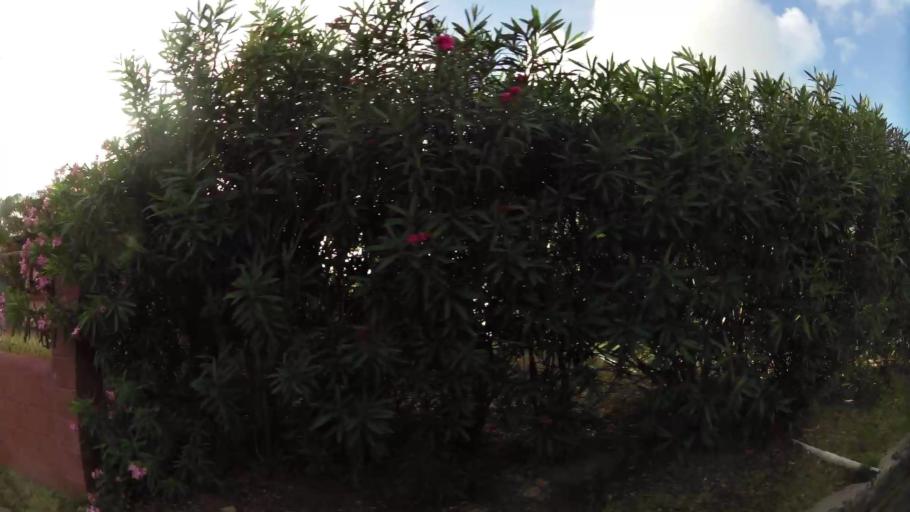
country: AG
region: Saint George
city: Piggotts
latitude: 17.1635
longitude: -61.8170
